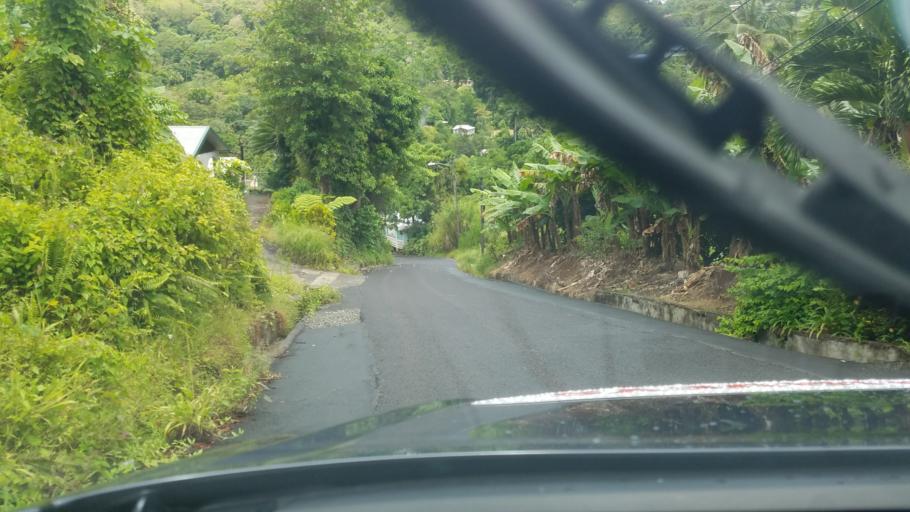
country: LC
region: Castries Quarter
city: Bisee
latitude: 13.9999
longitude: -60.9614
